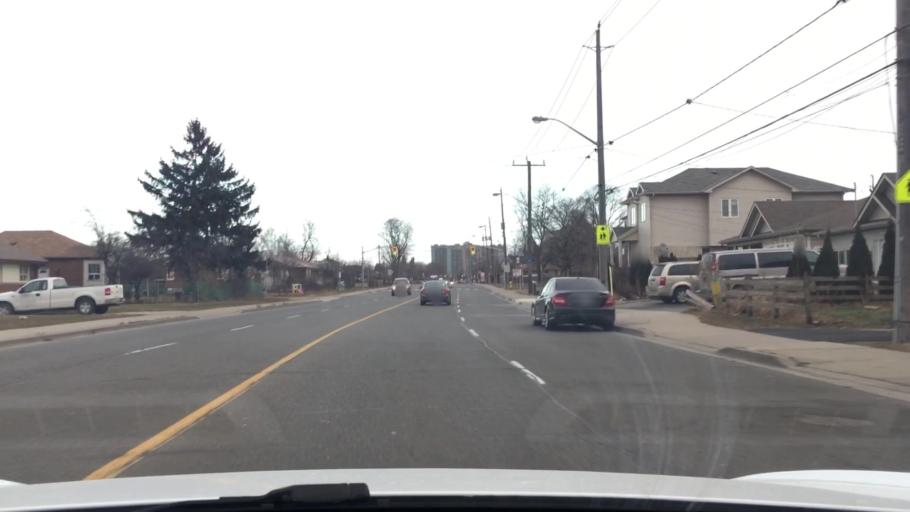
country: CA
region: Ontario
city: Scarborough
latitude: 43.7182
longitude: -79.2592
